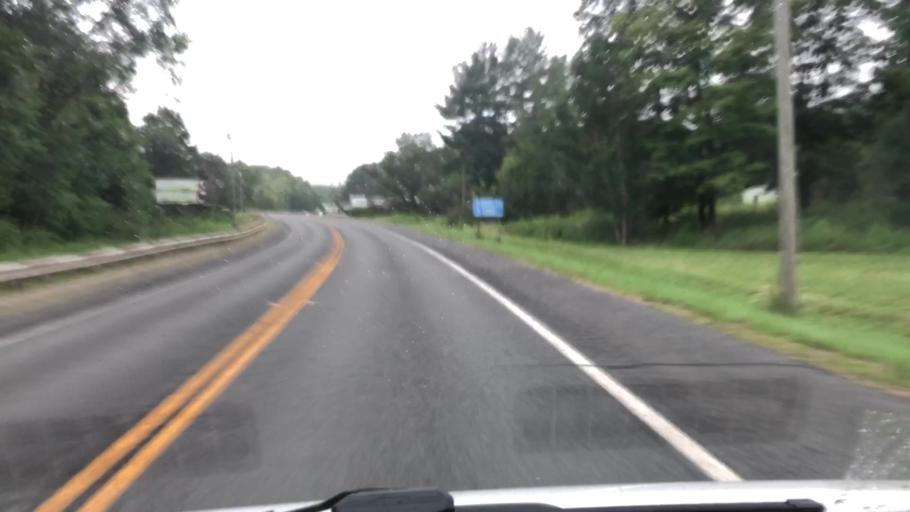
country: US
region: Massachusetts
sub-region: Berkshire County
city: Lanesborough
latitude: 42.6055
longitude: -73.2380
